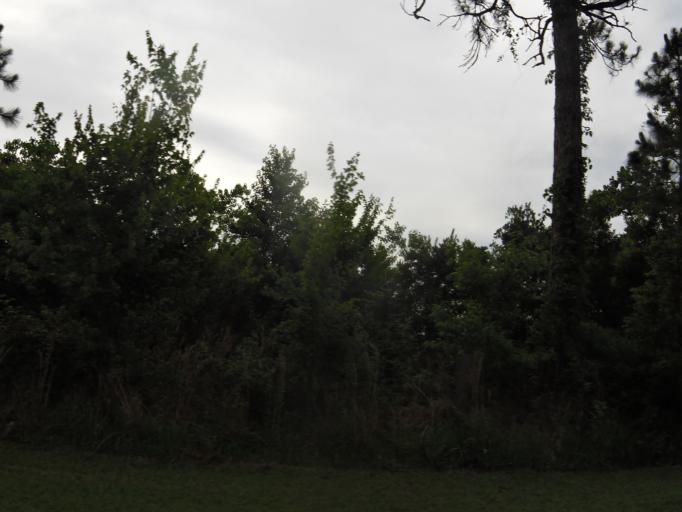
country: US
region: Florida
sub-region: Nassau County
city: Nassau Village-Ratliff
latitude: 30.5219
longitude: -81.7466
